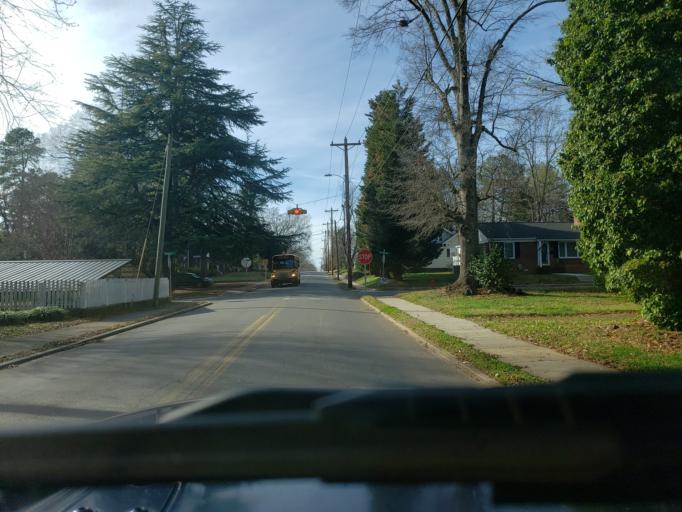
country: US
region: North Carolina
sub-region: Cleveland County
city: Kings Mountain
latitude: 35.2381
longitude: -81.3507
